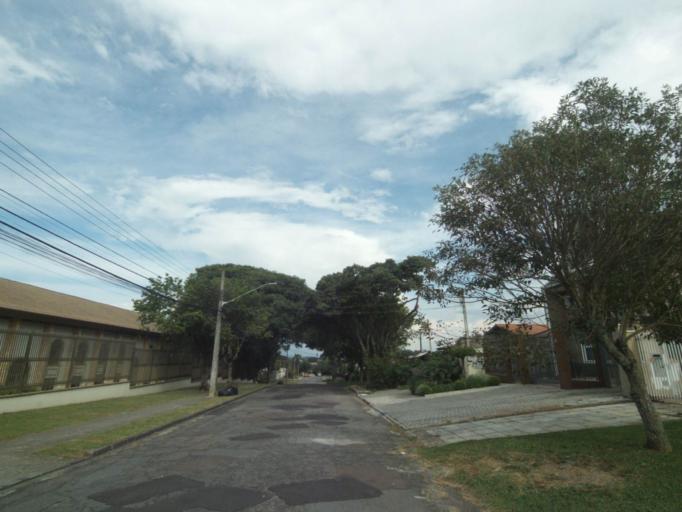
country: BR
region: Parana
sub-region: Pinhais
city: Pinhais
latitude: -25.4439
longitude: -49.2202
